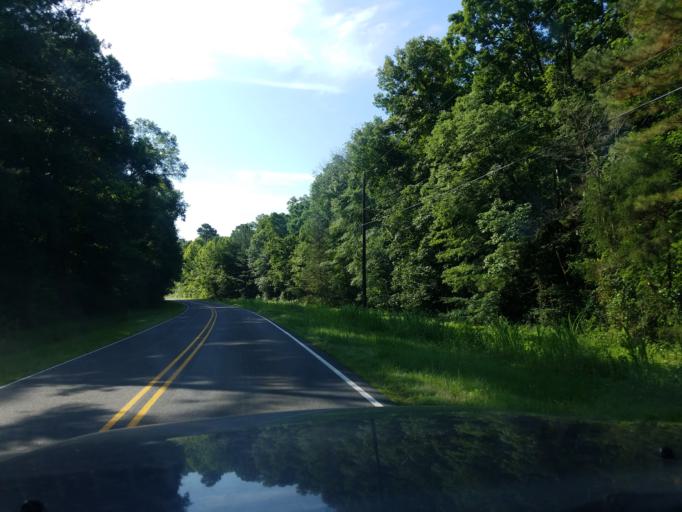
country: US
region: North Carolina
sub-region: Granville County
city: Butner
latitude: 36.1805
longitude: -78.8054
